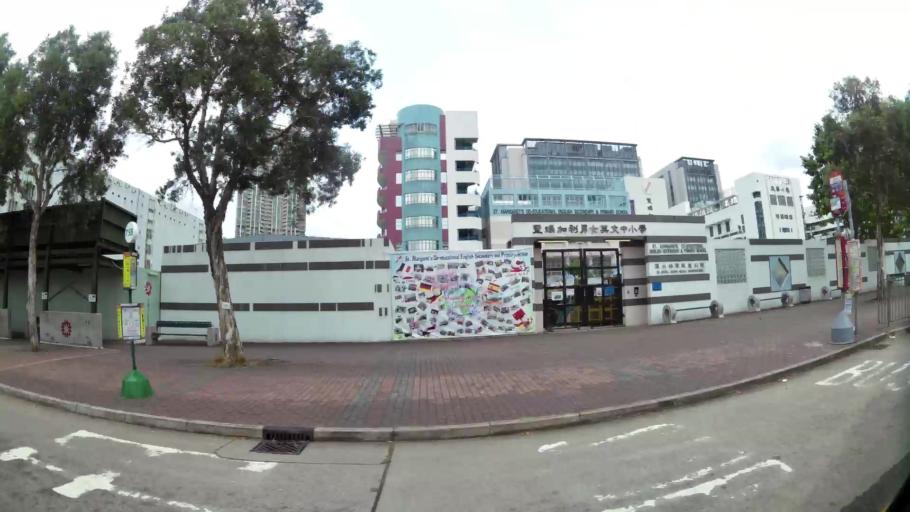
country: HK
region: Sham Shui Po
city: Sham Shui Po
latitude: 22.3301
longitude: 114.1512
